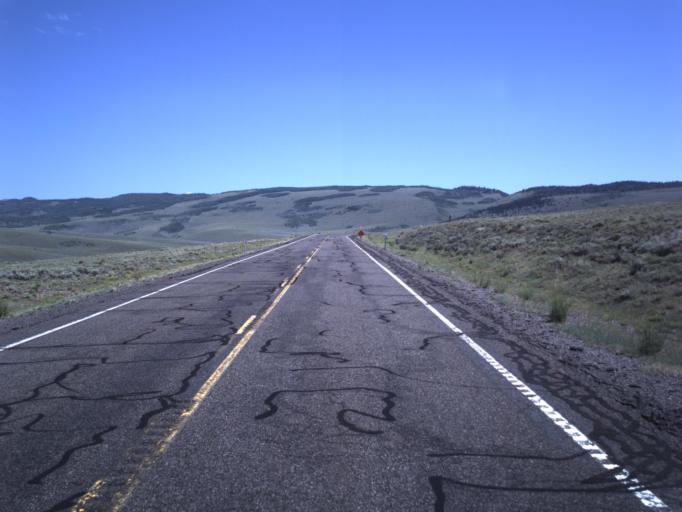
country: US
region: Utah
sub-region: Wayne County
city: Loa
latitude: 38.5651
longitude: -111.5013
